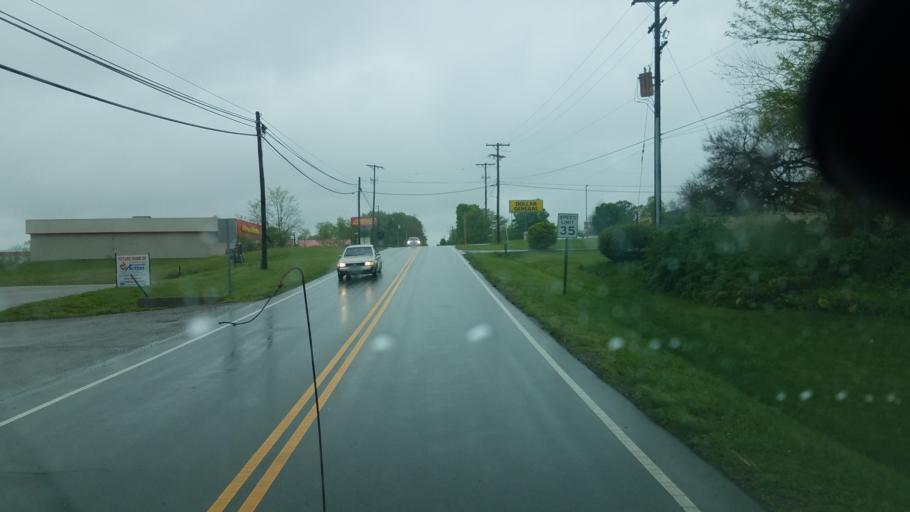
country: US
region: Ohio
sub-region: Highland County
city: Greenfield
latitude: 39.3479
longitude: -83.4009
